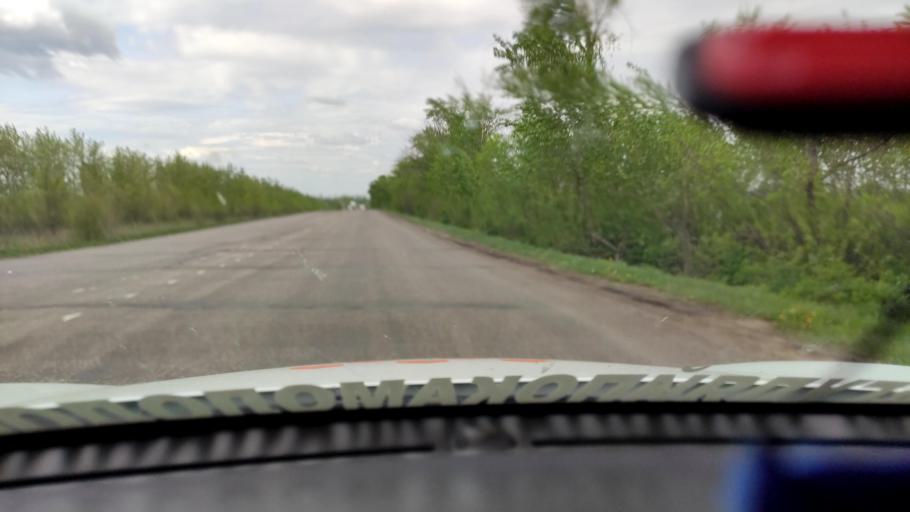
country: RU
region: Voronezj
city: Maslovka
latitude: 51.4937
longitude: 39.3083
